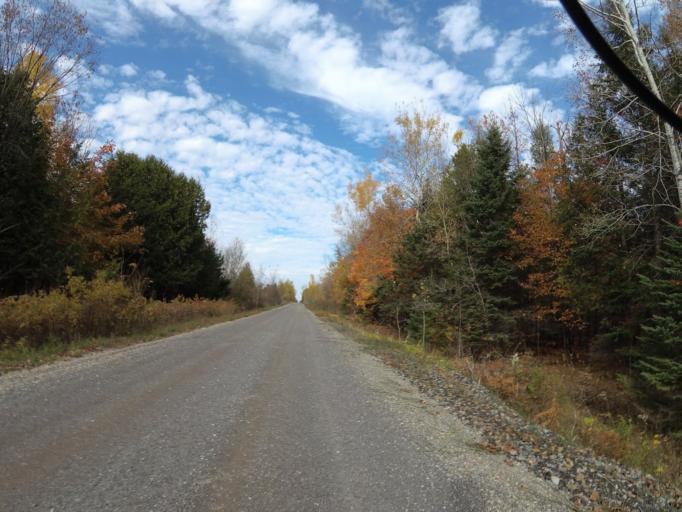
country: CA
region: Ontario
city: Carleton Place
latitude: 45.0613
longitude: -76.0942
